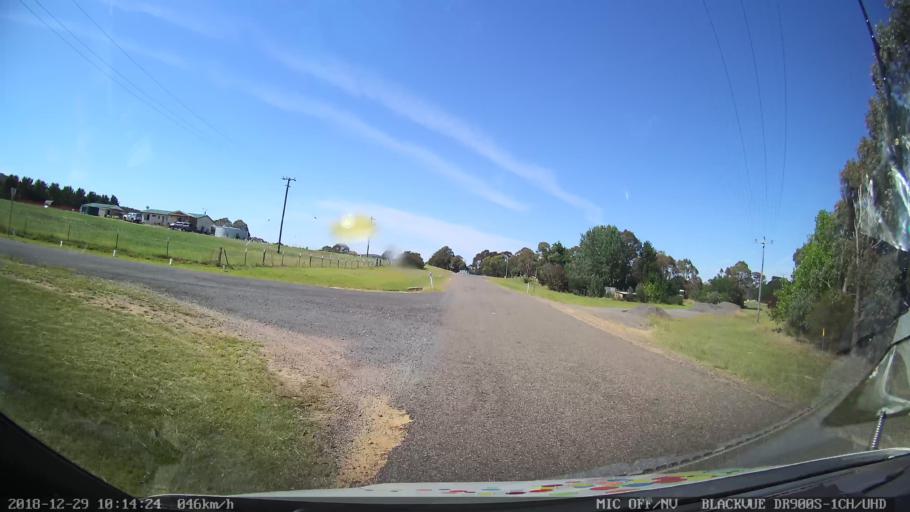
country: AU
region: New South Wales
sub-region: Yass Valley
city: Gundaroo
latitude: -34.9117
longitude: 149.4392
